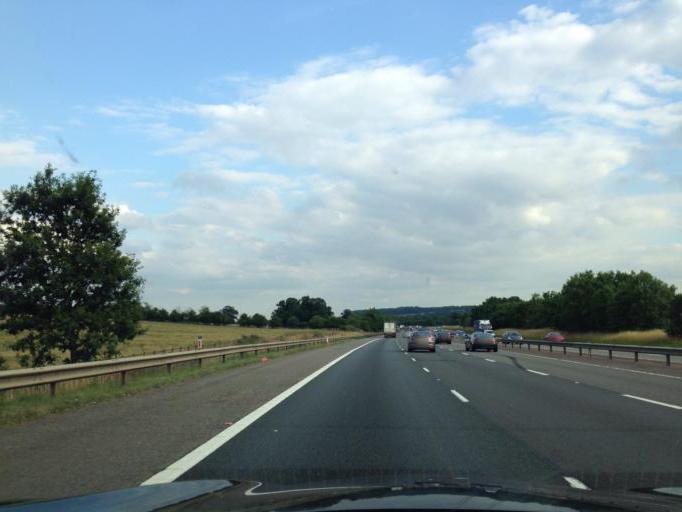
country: GB
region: England
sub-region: Oxfordshire
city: Hanwell
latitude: 52.1483
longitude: -1.4179
